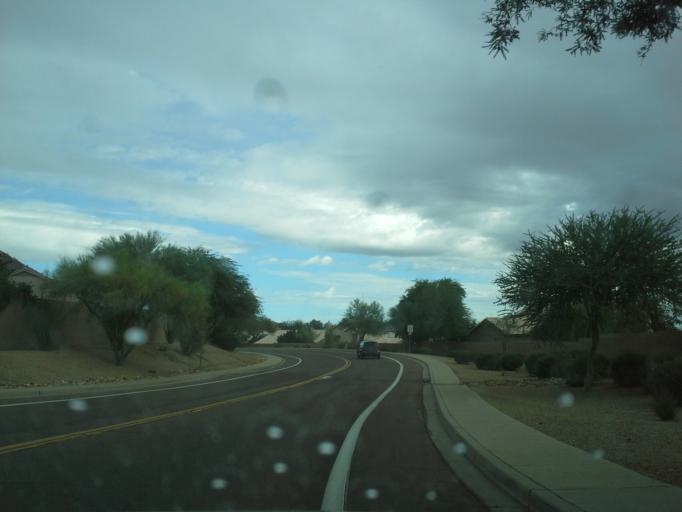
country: US
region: Arizona
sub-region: Maricopa County
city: Paradise Valley
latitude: 33.6139
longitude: -112.0461
